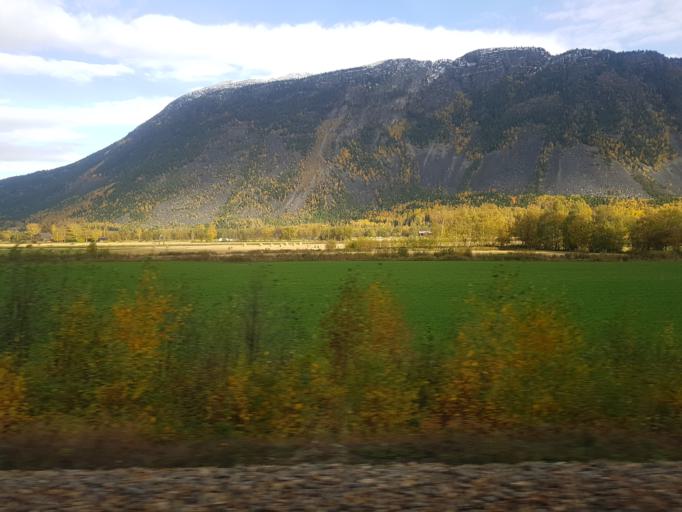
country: NO
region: Oppland
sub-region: Sel
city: Otta
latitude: 61.8386
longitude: 9.4768
